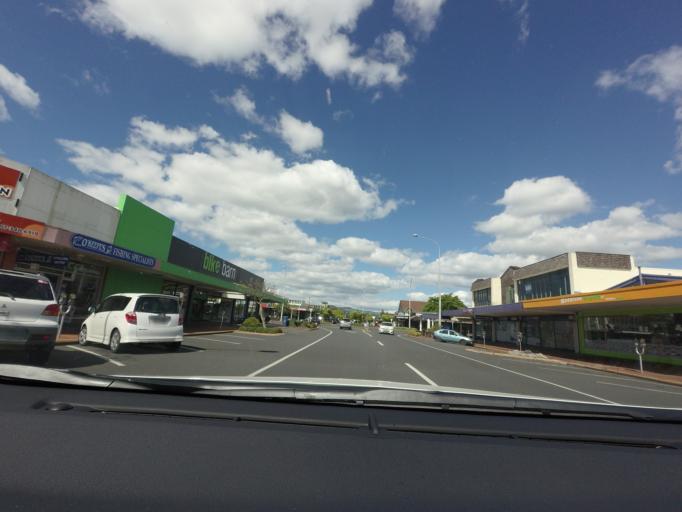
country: NZ
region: Bay of Plenty
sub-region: Rotorua District
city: Rotorua
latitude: -38.1389
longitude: 176.2531
